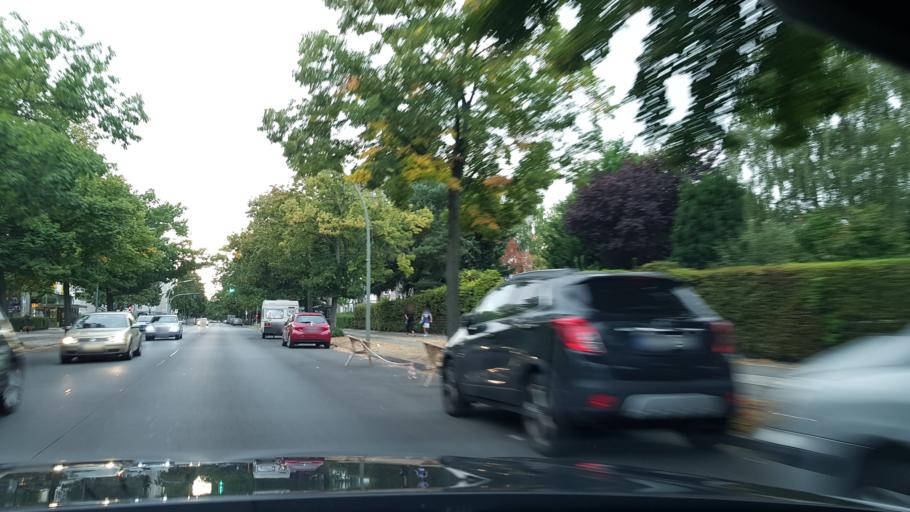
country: DE
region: Berlin
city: Reinickendorf
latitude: 52.5630
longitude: 13.3445
